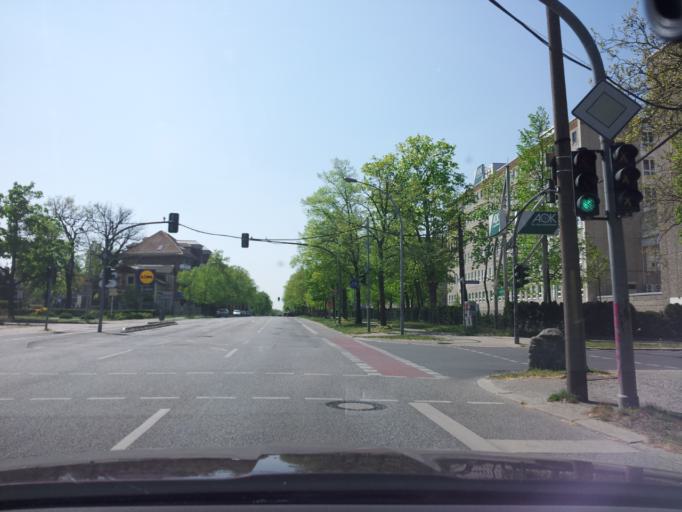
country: DE
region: Brandenburg
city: Teltow
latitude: 52.4009
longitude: 13.2527
